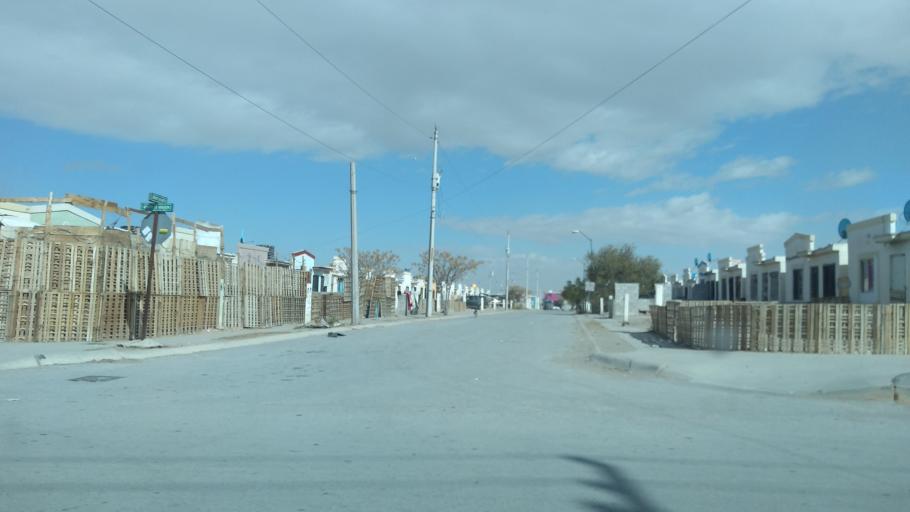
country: US
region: Texas
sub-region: El Paso County
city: San Elizario
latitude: 31.5641
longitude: -106.3370
